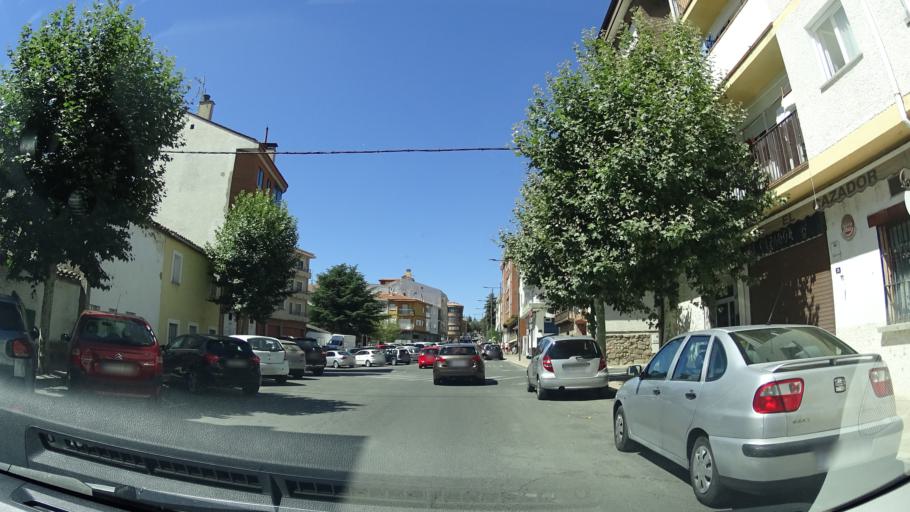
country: ES
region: Castille and Leon
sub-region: Provincia de Avila
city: Las Navas del Marques
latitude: 40.6034
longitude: -4.3328
